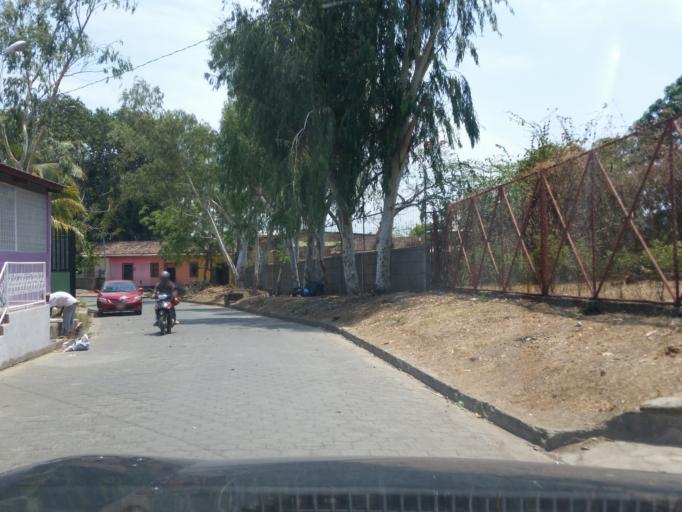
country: NI
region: Granada
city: Granada
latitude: 11.9366
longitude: -85.9543
